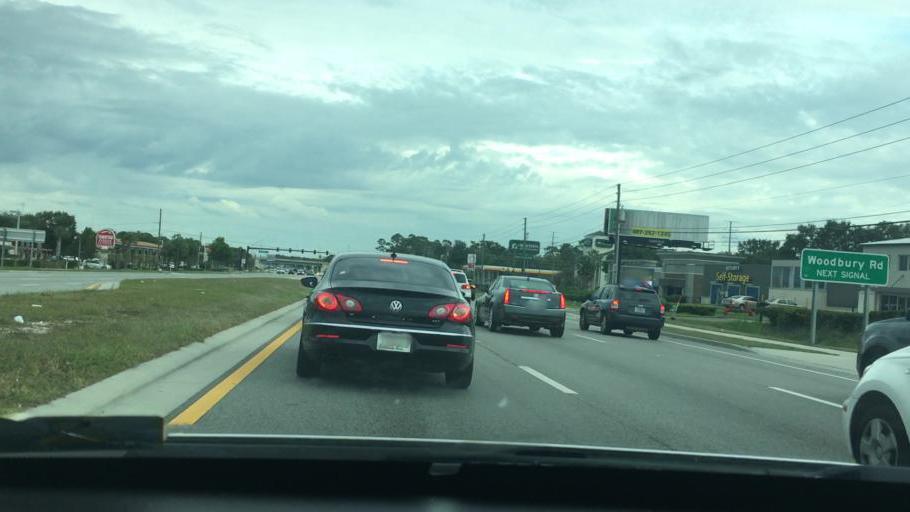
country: US
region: Florida
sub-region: Orange County
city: Alafaya
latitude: 28.5656
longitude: -81.1979
